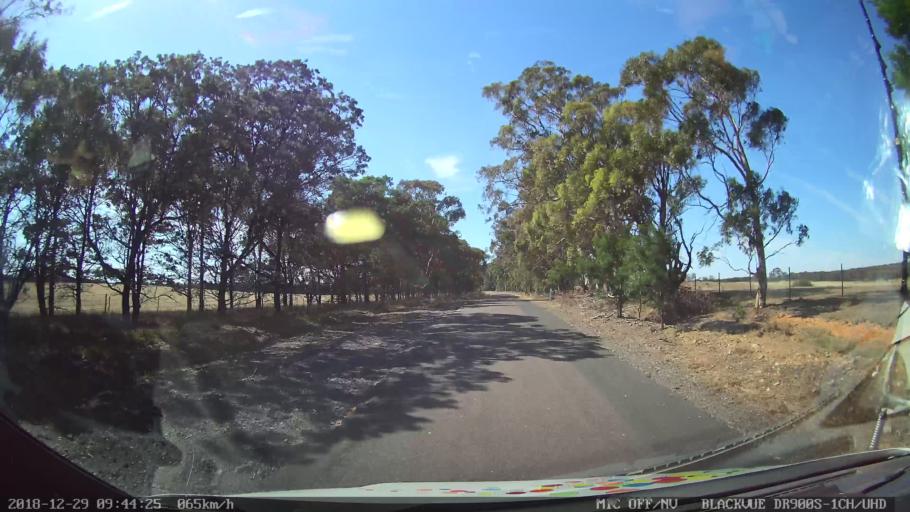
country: AU
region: New South Wales
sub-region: Upper Lachlan Shire
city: Crookwell
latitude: -34.6890
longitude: 149.4264
